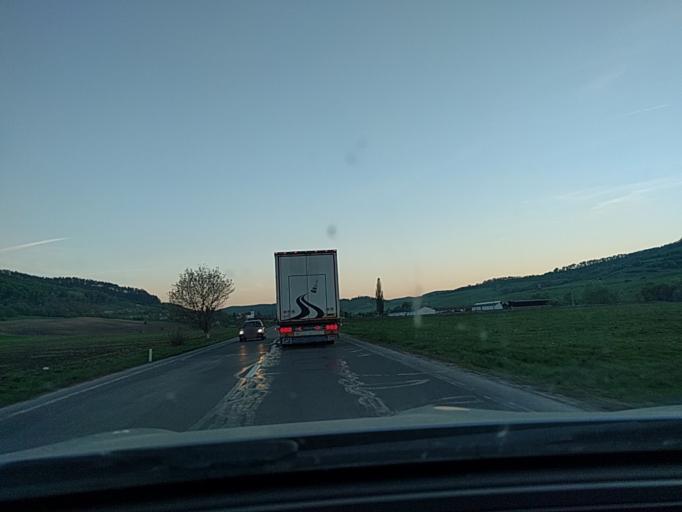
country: RO
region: Mures
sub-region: Comuna Balauseri
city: Chendu
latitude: 46.3639
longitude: 24.7214
